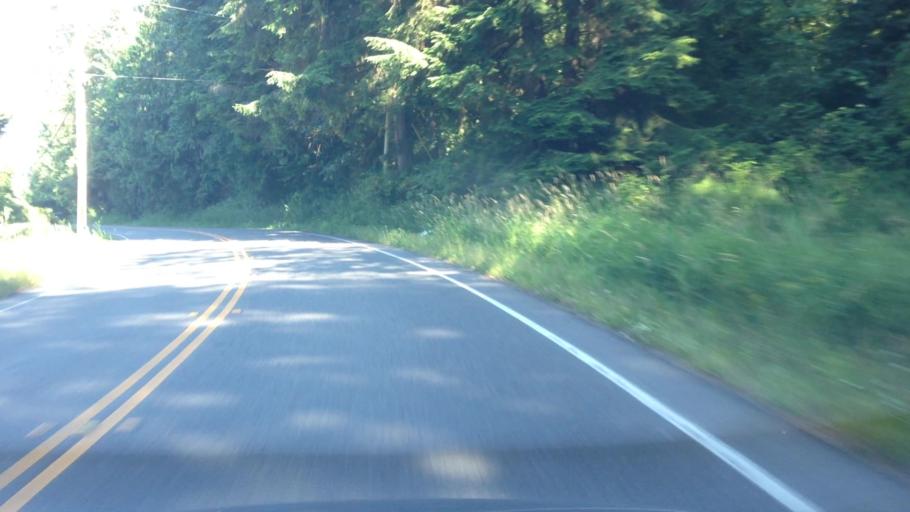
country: US
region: Washington
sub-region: King County
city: Duvall
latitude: 47.7469
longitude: -121.9603
